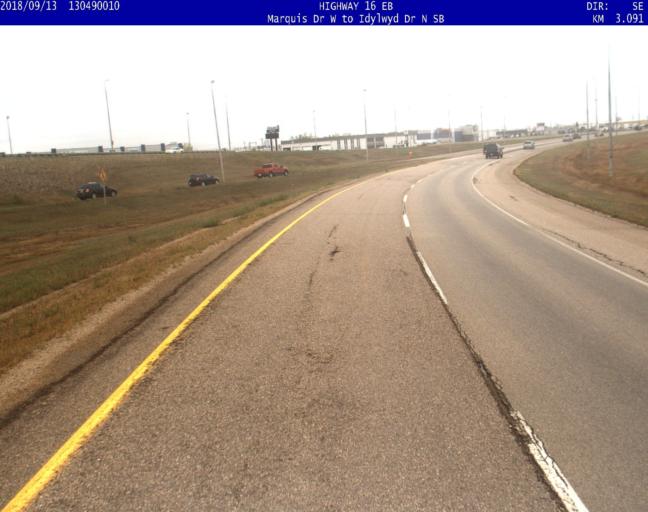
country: CA
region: Saskatchewan
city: Saskatoon
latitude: 52.1829
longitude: -106.6724
